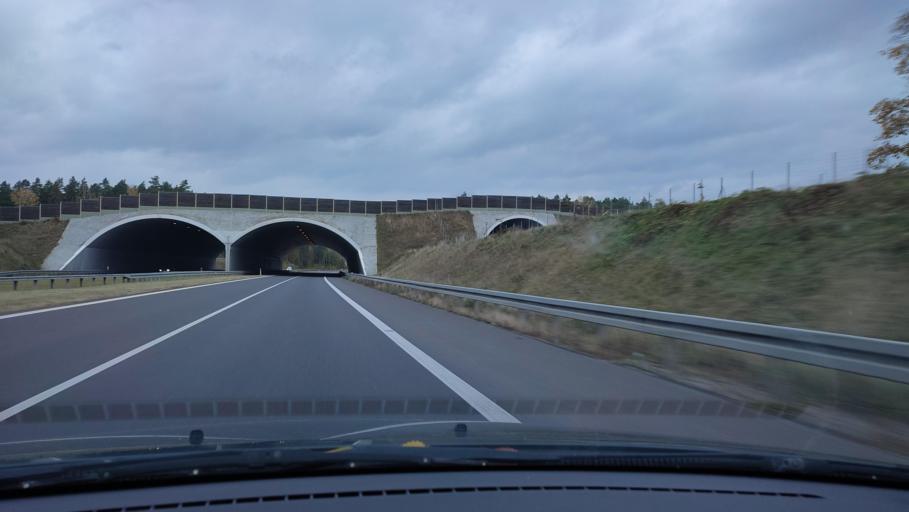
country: PL
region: Masovian Voivodeship
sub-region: Powiat mlawski
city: Wieczfnia Koscielna
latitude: 53.2510
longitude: 20.4242
